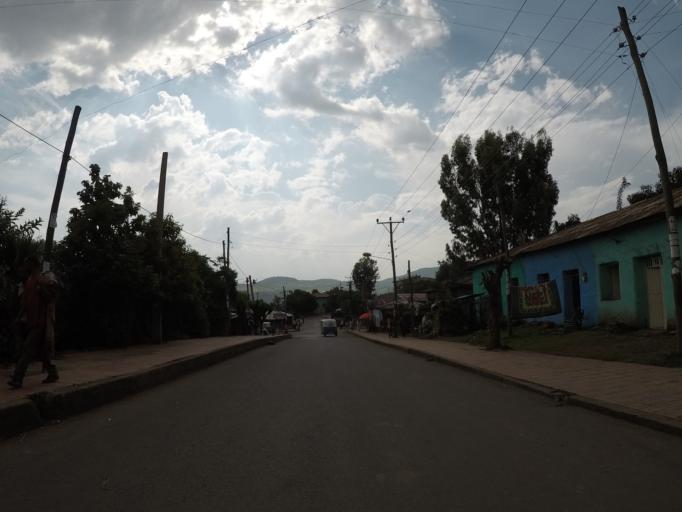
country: ET
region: Amhara
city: Gondar
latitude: 12.6152
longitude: 37.4707
